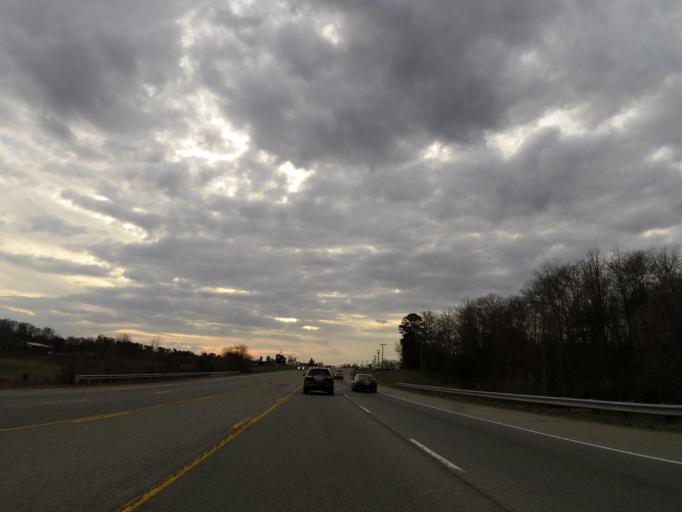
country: US
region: Tennessee
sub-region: Loudon County
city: Greenback
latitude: 35.6732
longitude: -84.0856
